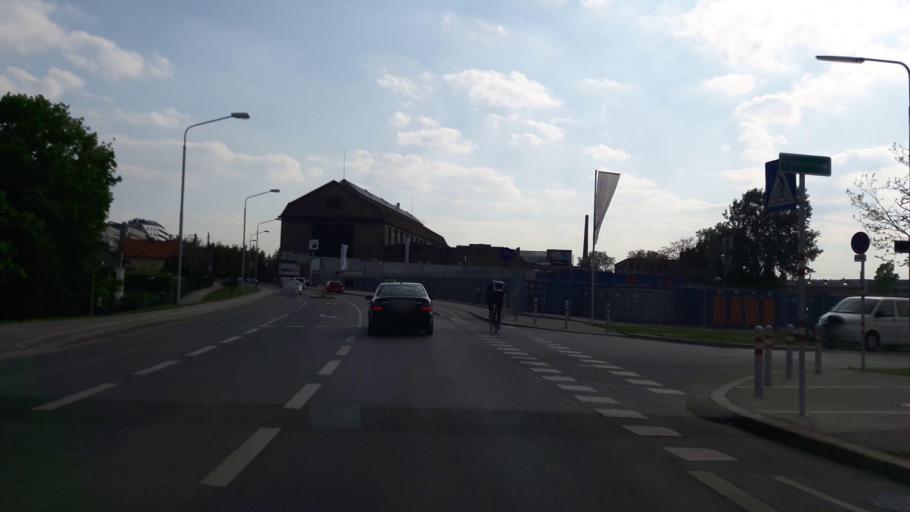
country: AT
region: Lower Austria
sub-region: Politischer Bezirk Wien-Umgebung
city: Gerasdorf bei Wien
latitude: 48.2341
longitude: 16.4595
